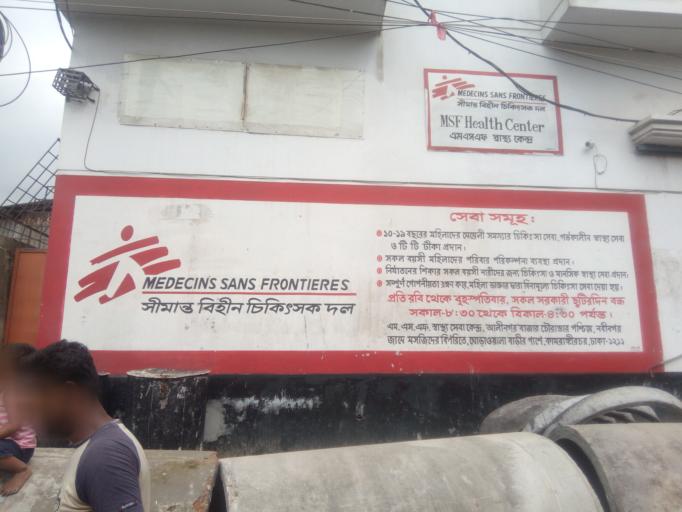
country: BD
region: Dhaka
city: Azimpur
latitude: 23.7160
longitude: 90.3675
